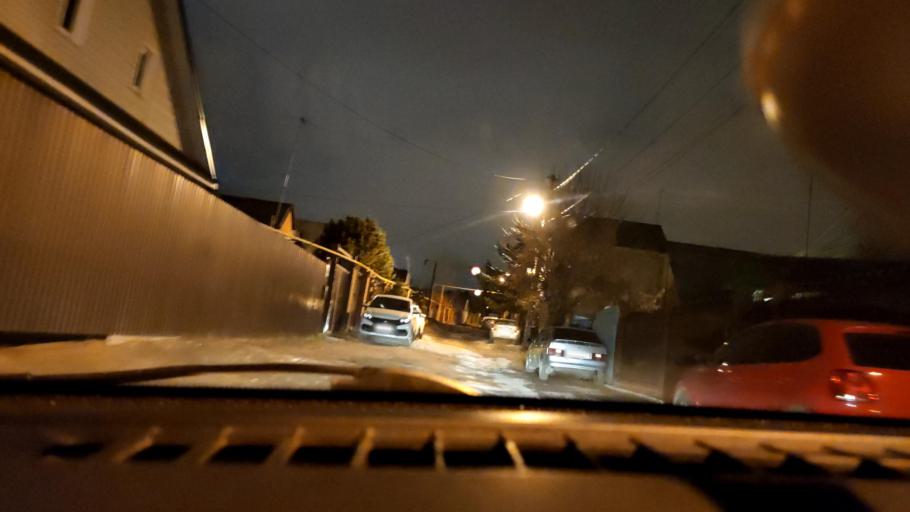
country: RU
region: Samara
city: Samara
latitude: 53.1801
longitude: 50.1531
